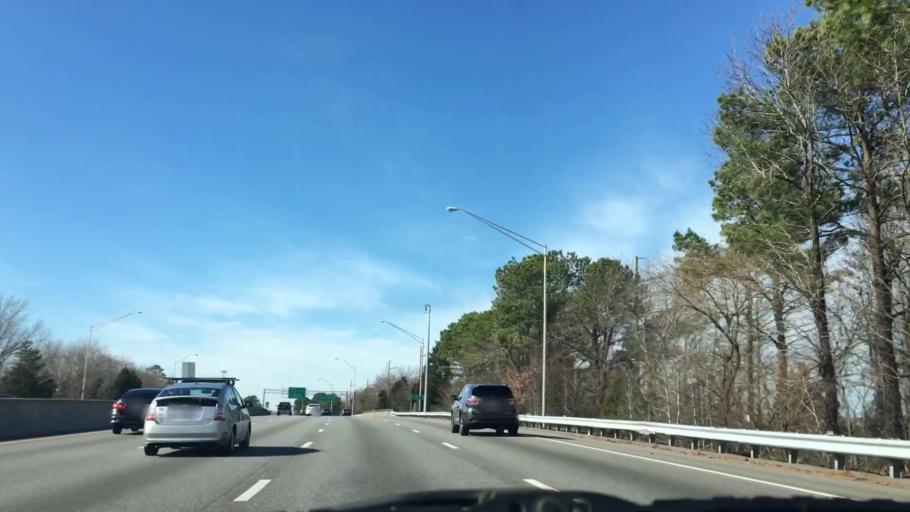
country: US
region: Virginia
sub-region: City of Virginia Beach
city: Virginia Beach
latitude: 36.8349
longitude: -76.0878
